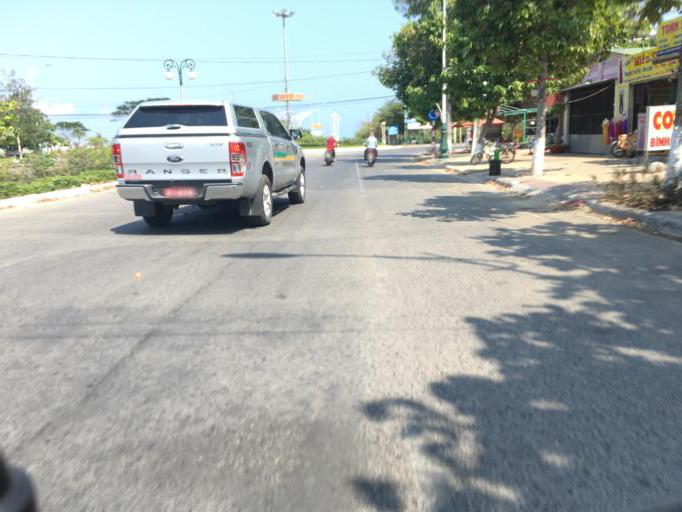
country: VN
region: Ninh Thuan
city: Phan Rang-Thap Cham
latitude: 11.5629
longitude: 109.0208
